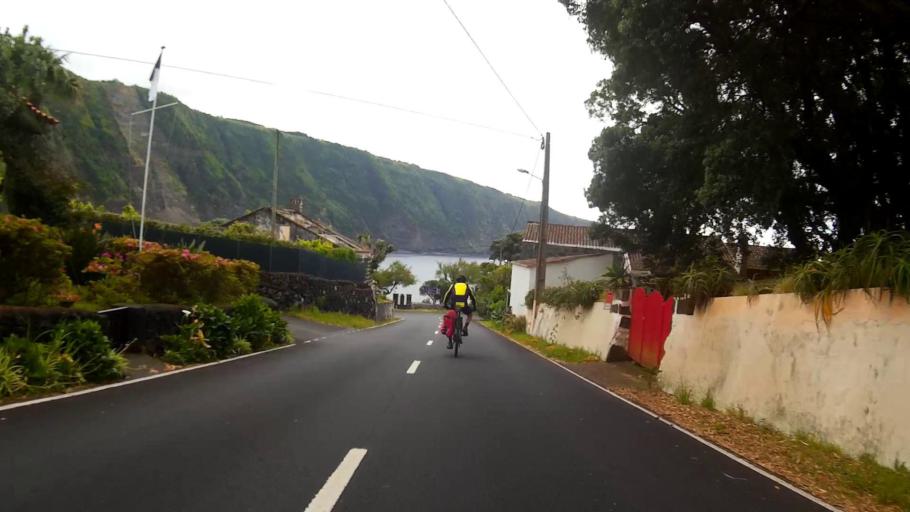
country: PT
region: Azores
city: Ribeira Grande
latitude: 38.5664
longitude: -28.7734
